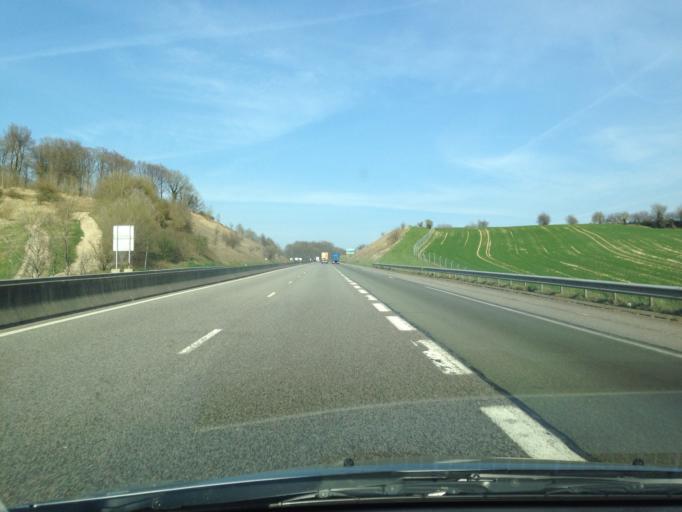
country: FR
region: Haute-Normandie
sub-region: Departement de la Seine-Maritime
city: Neufchatel-en-Bray
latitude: 49.7304
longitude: 1.4604
